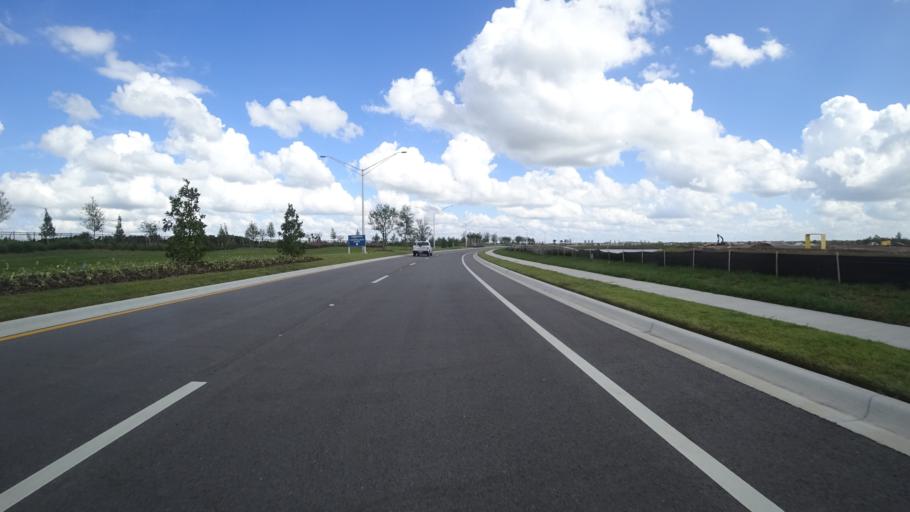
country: US
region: Florida
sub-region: Sarasota County
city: The Meadows
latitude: 27.4495
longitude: -82.3651
